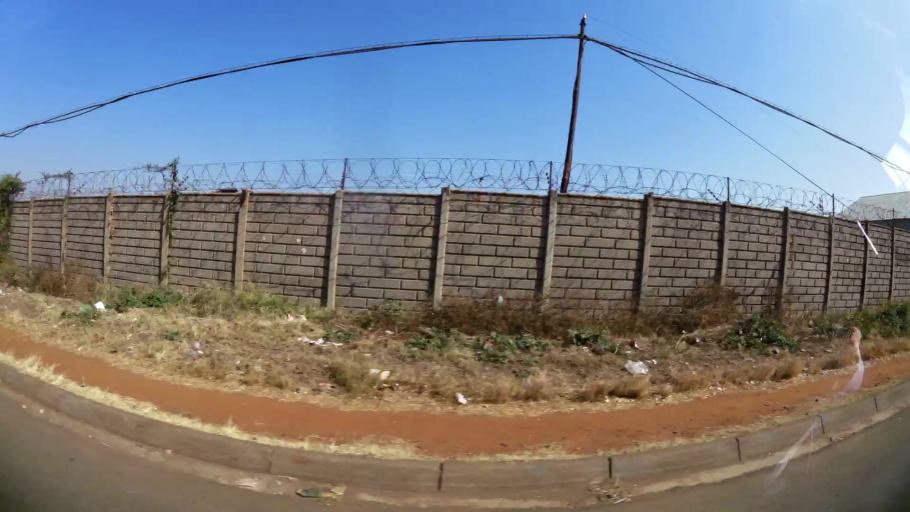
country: ZA
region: Gauteng
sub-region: Ekurhuleni Metropolitan Municipality
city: Boksburg
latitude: -26.1738
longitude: 28.2122
